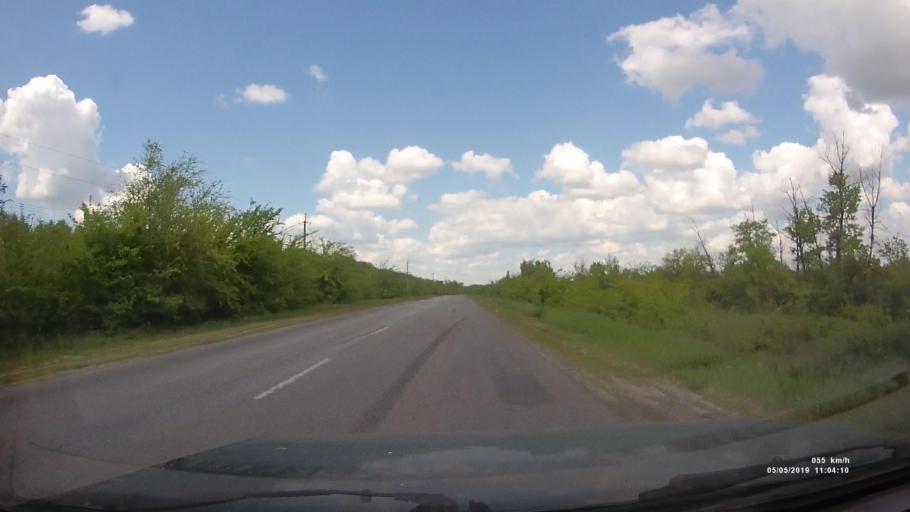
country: RU
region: Rostov
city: Ust'-Donetskiy
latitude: 47.6955
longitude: 40.9214
